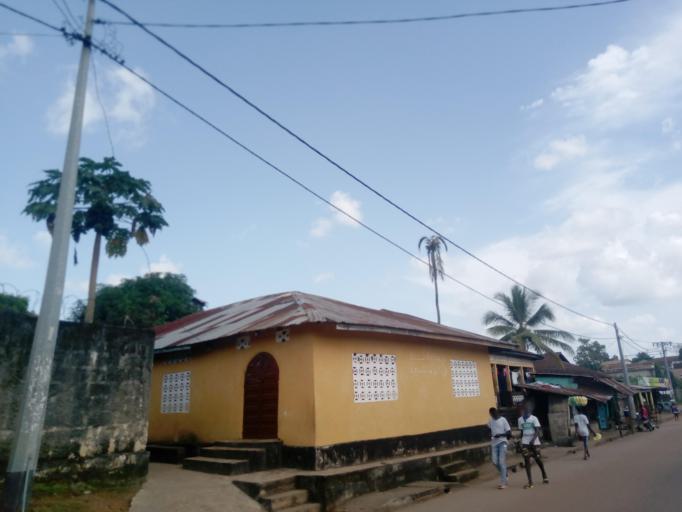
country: SL
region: Northern Province
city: Makeni
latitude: 8.8937
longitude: -12.0376
